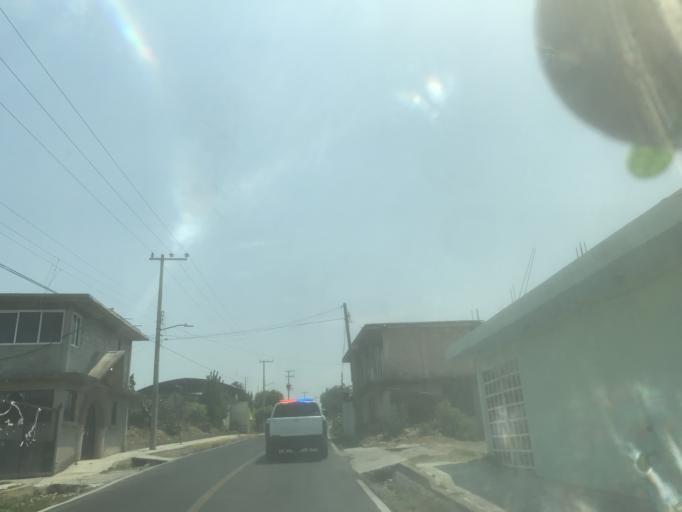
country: MX
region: Mexico
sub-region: Atlautla
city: San Andres Tlalamac
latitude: 18.9657
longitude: -98.8200
